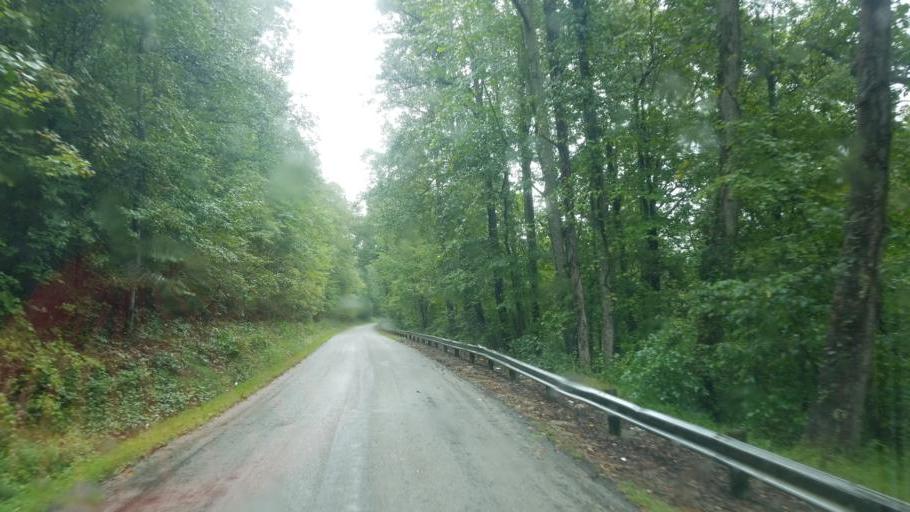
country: US
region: Ohio
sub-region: Scioto County
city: West Portsmouth
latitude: 38.7612
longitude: -83.1069
